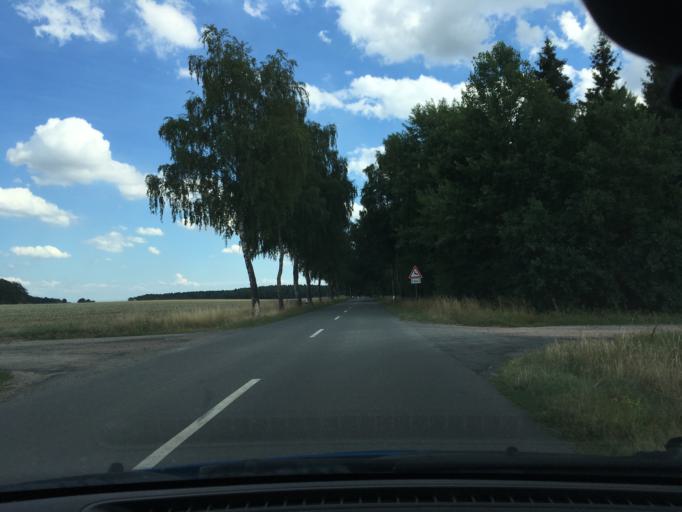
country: DE
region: Lower Saxony
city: Rehlingen
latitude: 53.0552
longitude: 10.2445
